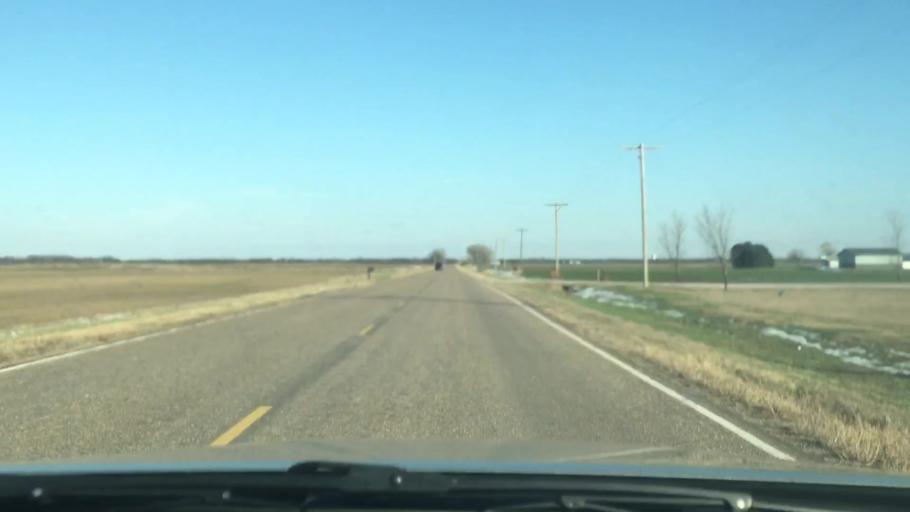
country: US
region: Kansas
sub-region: Rice County
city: Lyons
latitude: 38.2895
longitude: -98.1773
